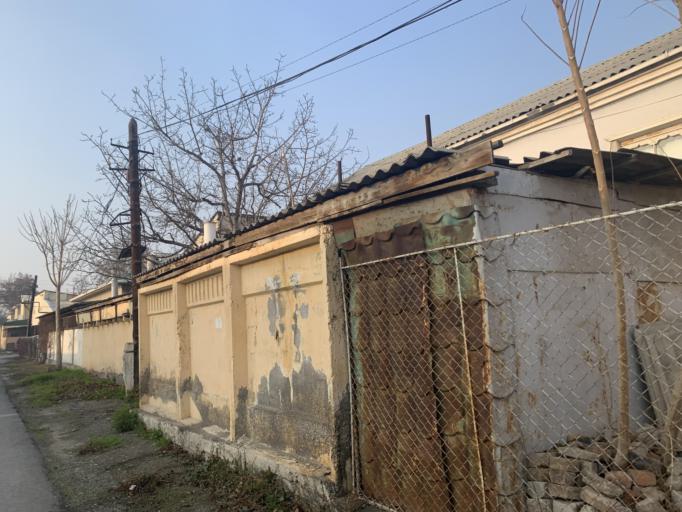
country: UZ
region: Fergana
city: Qo`qon
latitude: 40.5404
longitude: 70.9251
